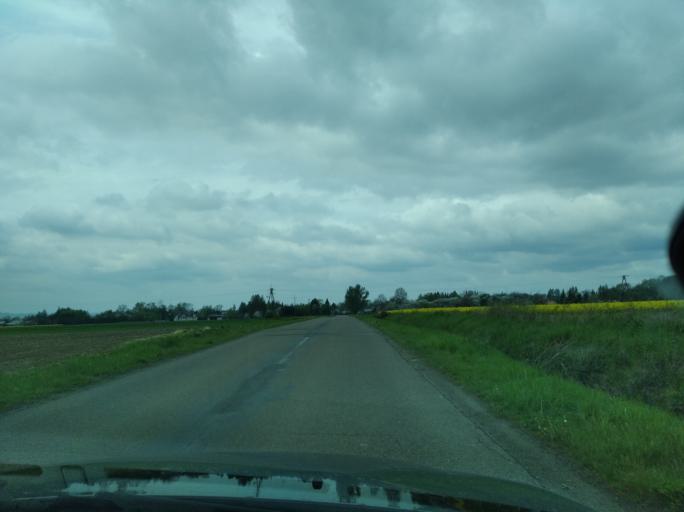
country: PL
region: Subcarpathian Voivodeship
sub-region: Powiat brzozowski
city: Gorki
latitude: 49.6174
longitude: 22.0273
